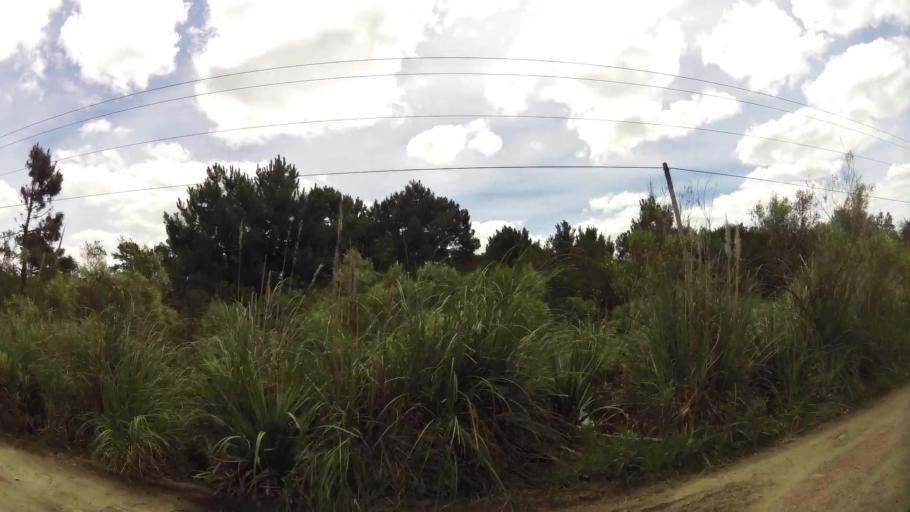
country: UY
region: Canelones
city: Pando
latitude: -34.8096
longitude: -55.9364
